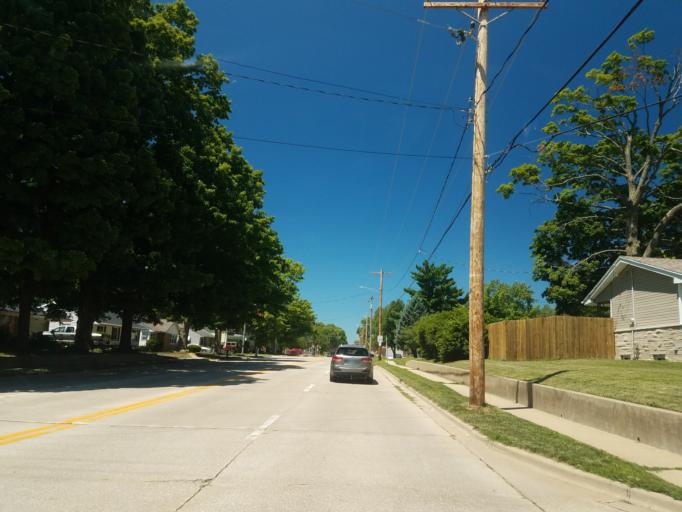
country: US
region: Illinois
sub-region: McLean County
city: Normal
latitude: 40.5099
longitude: -89.0016
